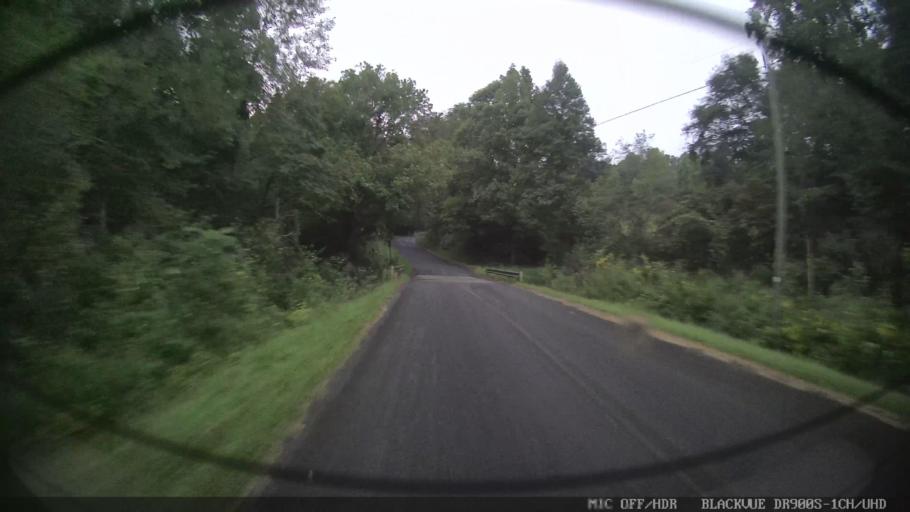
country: US
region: Georgia
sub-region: Gilmer County
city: Ellijay
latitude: 34.6843
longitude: -84.3333
